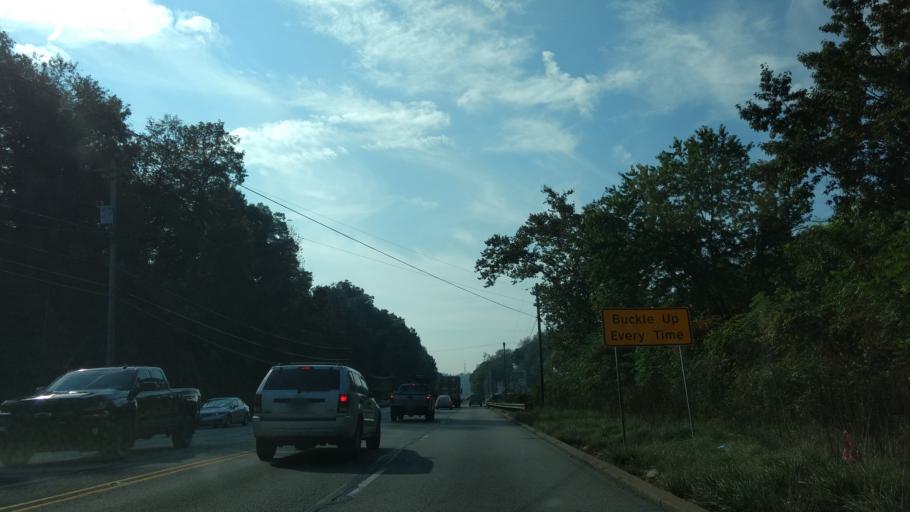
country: US
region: Pennsylvania
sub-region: Allegheny County
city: Pleasant Hills
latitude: 40.3204
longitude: -79.9419
